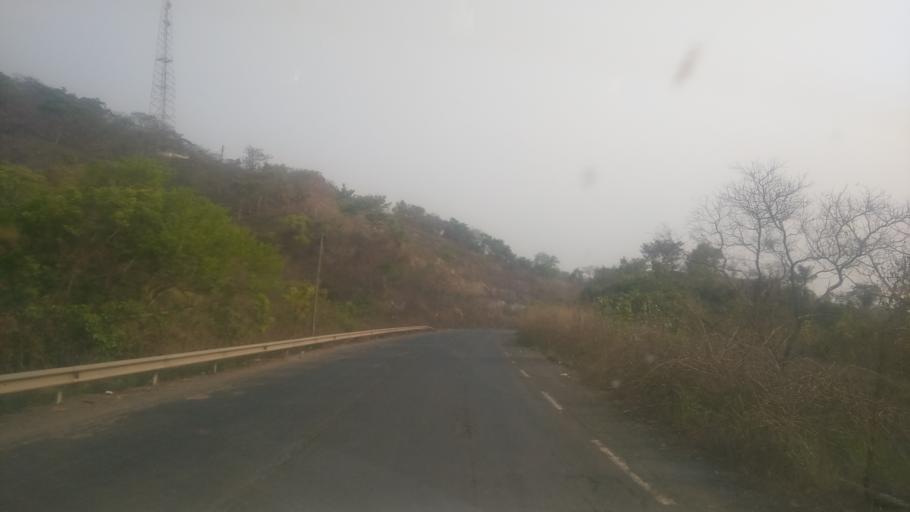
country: CM
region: West
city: Tonga
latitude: 5.0427
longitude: 10.7014
